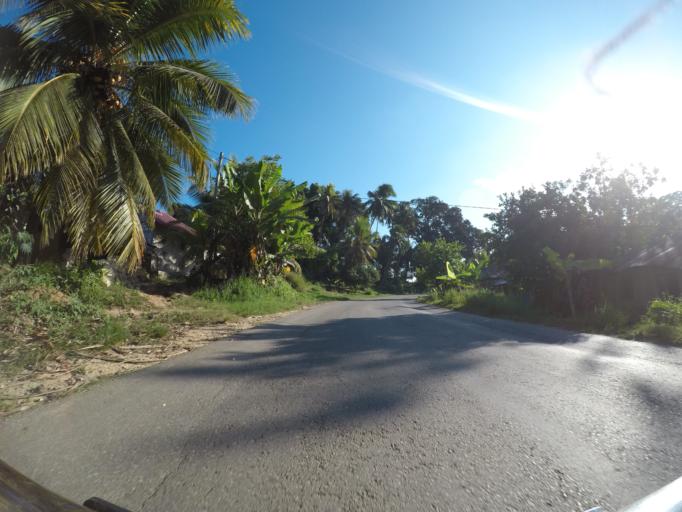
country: TZ
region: Pemba South
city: Chake Chake
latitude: -5.3045
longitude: 39.7523
